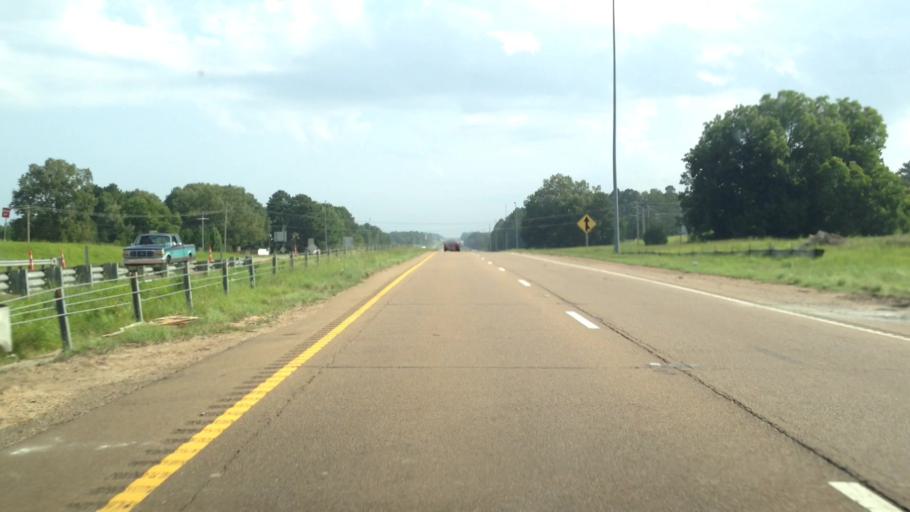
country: US
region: Mississippi
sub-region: Hinds County
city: Terry
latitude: 32.1014
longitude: -90.3025
